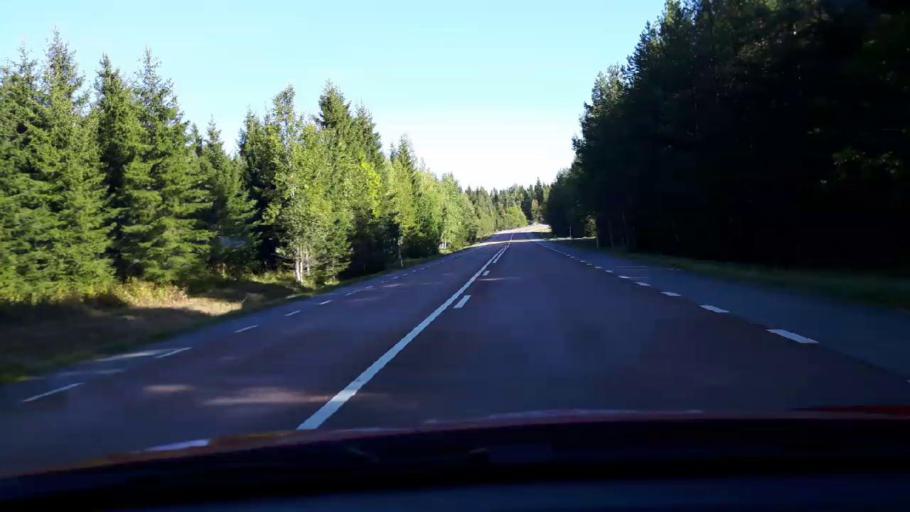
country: SE
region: Jaemtland
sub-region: OEstersunds Kommun
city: Brunflo
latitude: 62.9460
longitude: 15.0837
